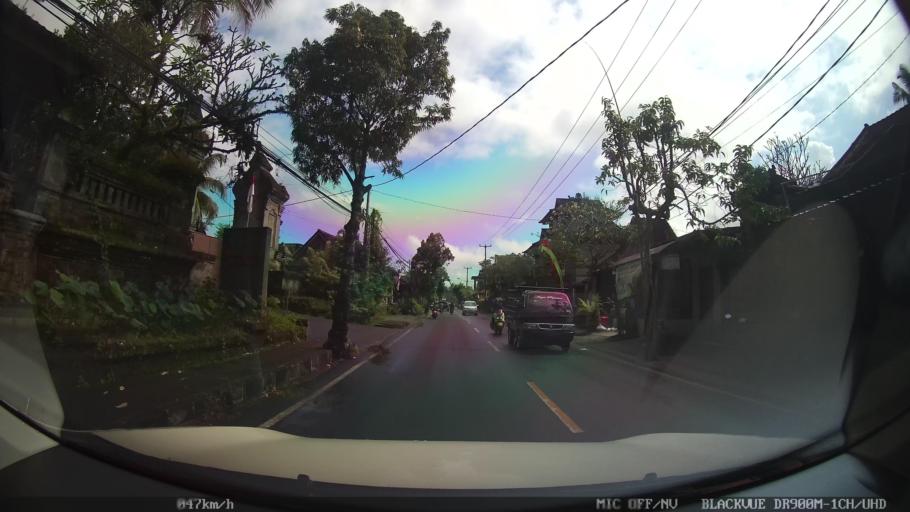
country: ID
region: Bali
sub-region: Kabupaten Gianyar
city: Ubud
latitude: -8.5364
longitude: 115.2725
